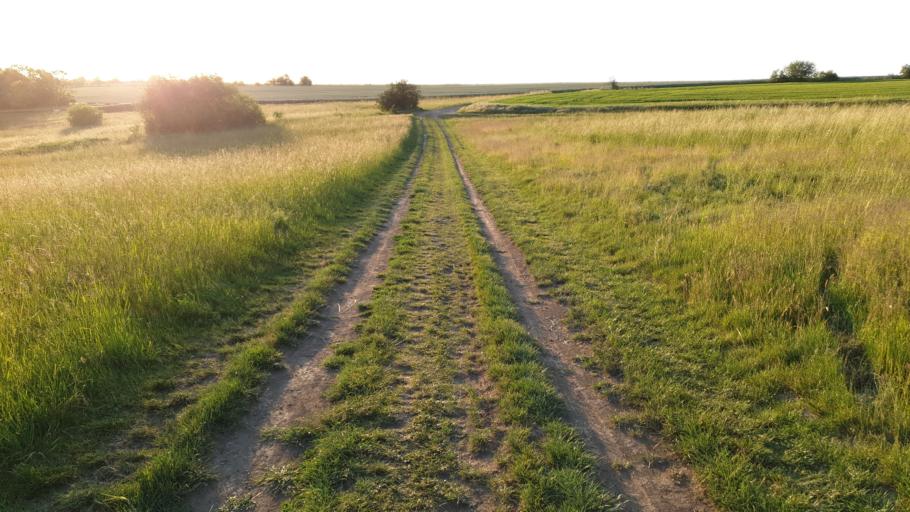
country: CZ
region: Central Bohemia
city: Rez
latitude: 50.1513
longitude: 14.3666
